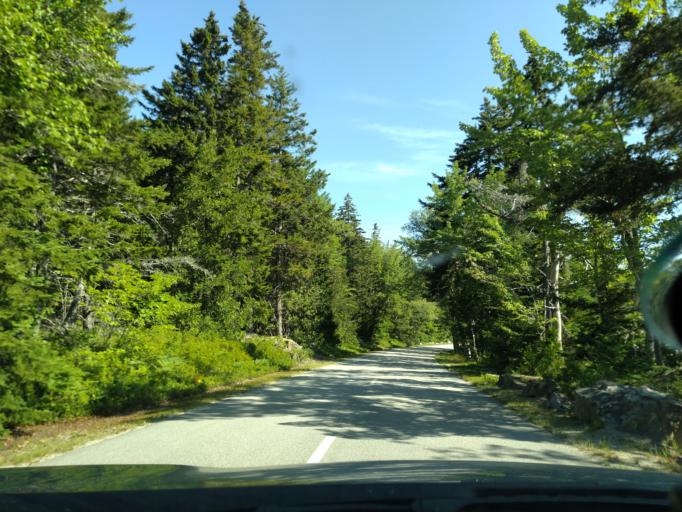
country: US
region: Maine
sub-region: Hancock County
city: Gouldsboro
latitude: 44.3594
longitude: -68.0468
